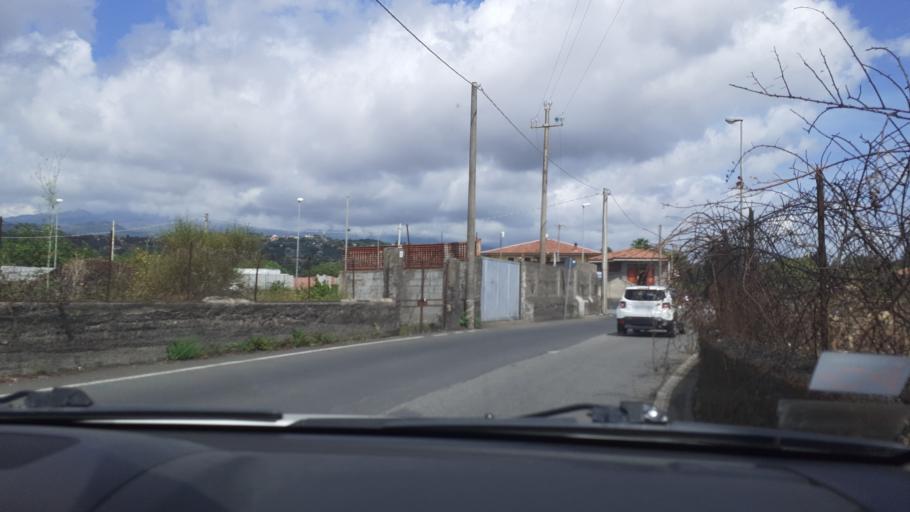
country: IT
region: Sicily
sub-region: Catania
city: San Giovanni la Punta
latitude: 37.5887
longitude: 15.0941
